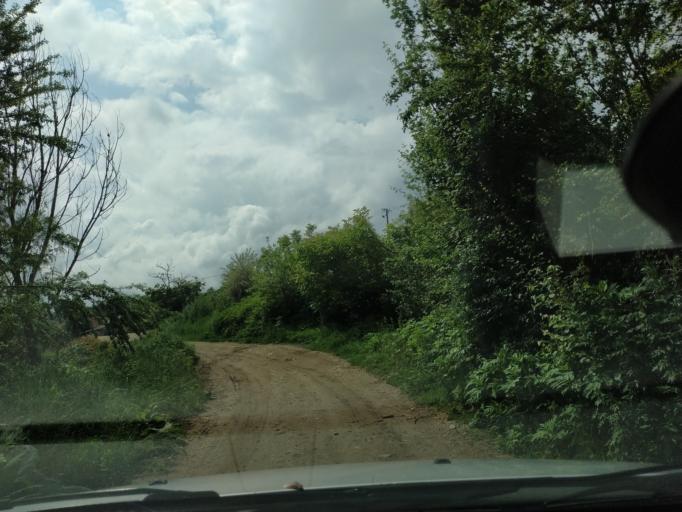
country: RS
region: Central Serbia
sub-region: Nisavski Okrug
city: Aleksinac
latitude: 43.4280
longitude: 21.5872
